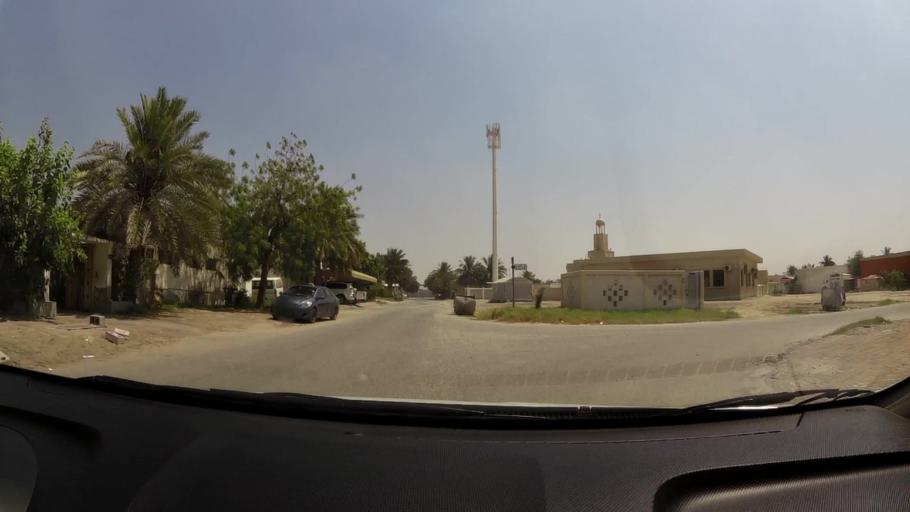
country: AE
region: Umm al Qaywayn
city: Umm al Qaywayn
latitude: 25.5619
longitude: 55.5570
